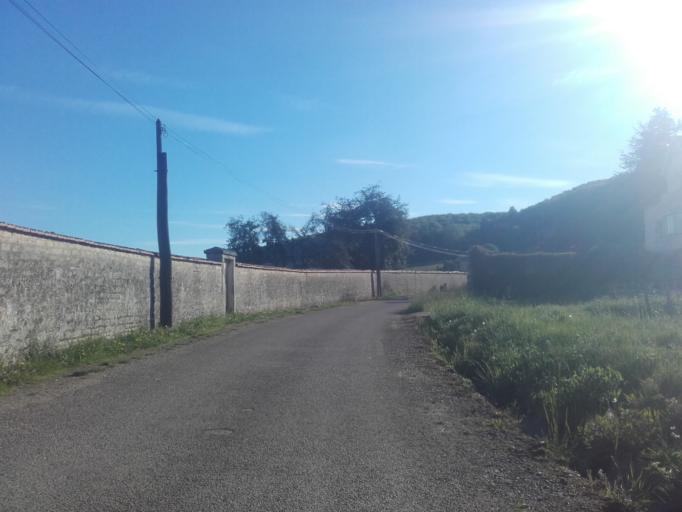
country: FR
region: Bourgogne
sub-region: Departement de Saone-et-Loire
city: Rully
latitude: 46.8762
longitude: 4.7353
